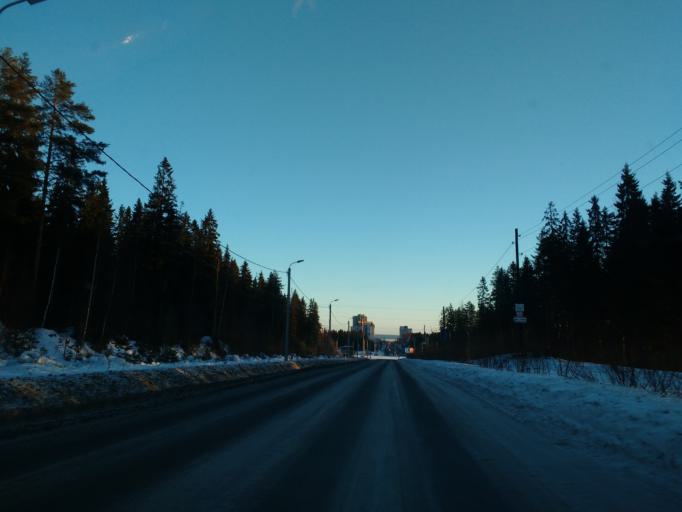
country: RU
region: Republic of Karelia
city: Petrozavodsk
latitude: 61.7770
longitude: 34.3028
